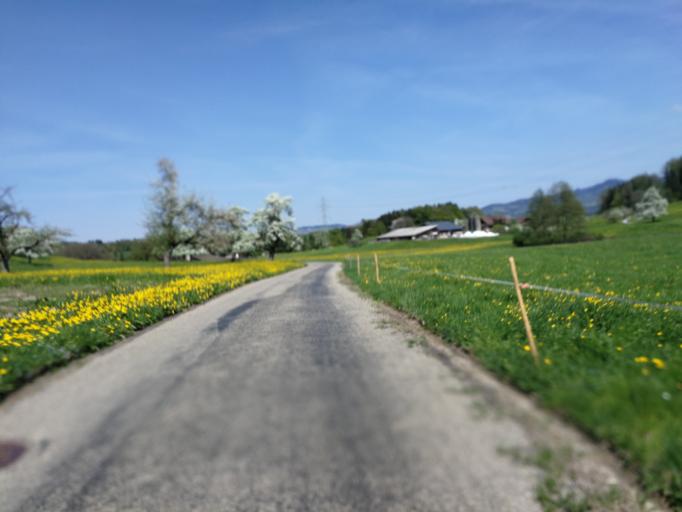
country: CH
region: Zurich
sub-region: Bezirk Hinwil
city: Wolfhausen
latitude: 47.2673
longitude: 8.7961
